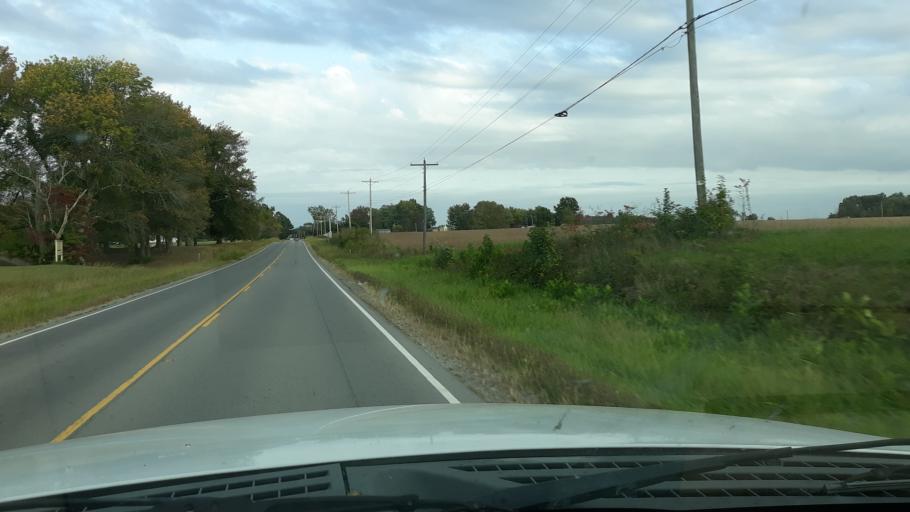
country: US
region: Illinois
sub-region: Saline County
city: Eldorado
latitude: 37.8215
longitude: -88.4900
